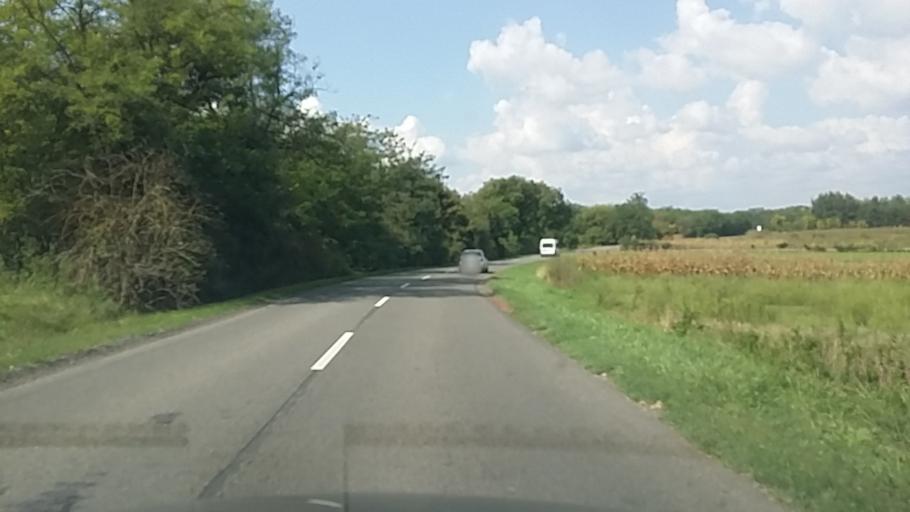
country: HU
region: Bacs-Kiskun
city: Tiszaalpar
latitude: 46.8273
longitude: 19.9776
